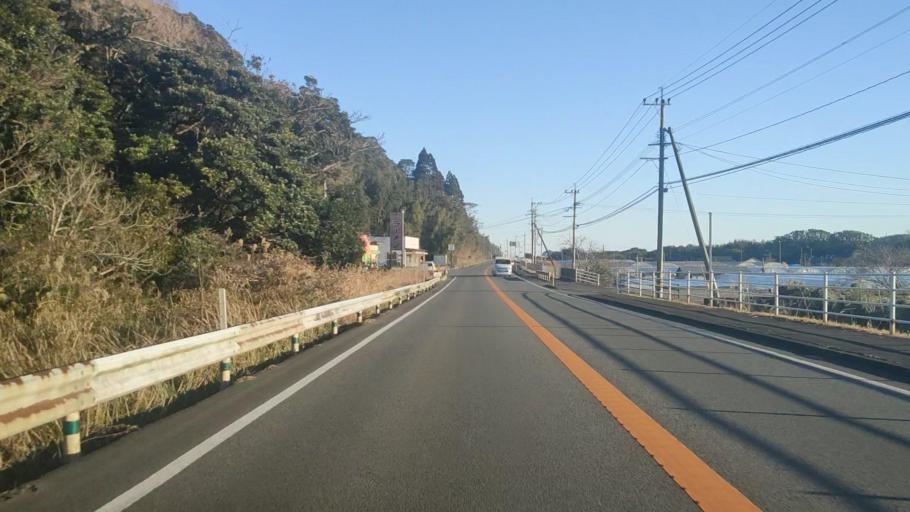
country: JP
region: Miyazaki
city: Takanabe
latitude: 32.0994
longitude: 131.5195
